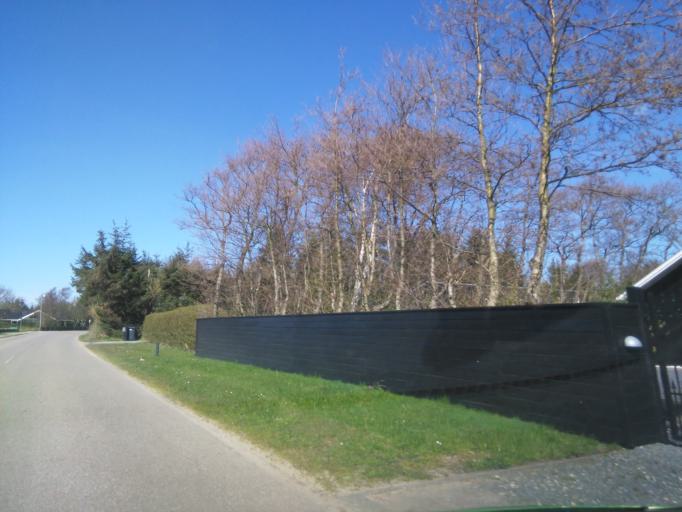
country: DK
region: South Denmark
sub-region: Varde Kommune
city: Oksbol
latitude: 55.5492
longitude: 8.1343
